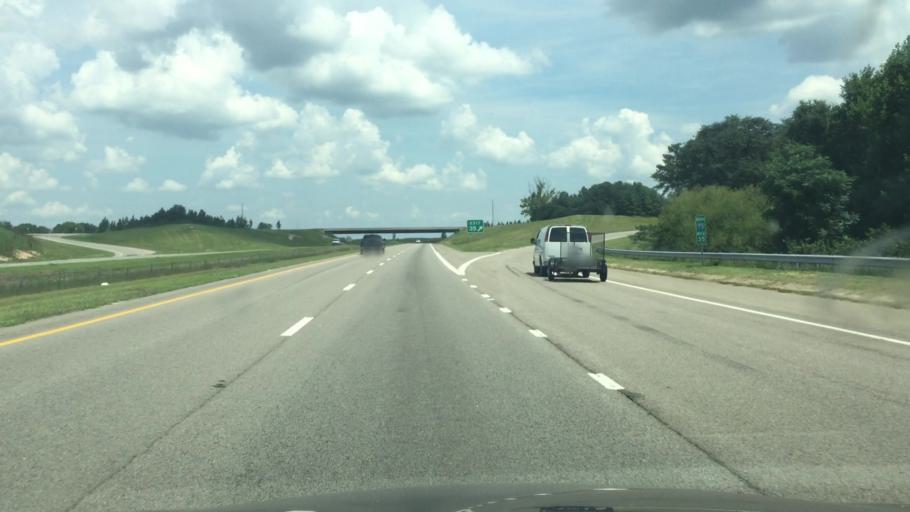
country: US
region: North Carolina
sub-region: Richmond County
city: Ellerbe
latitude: 35.1695
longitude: -79.7149
